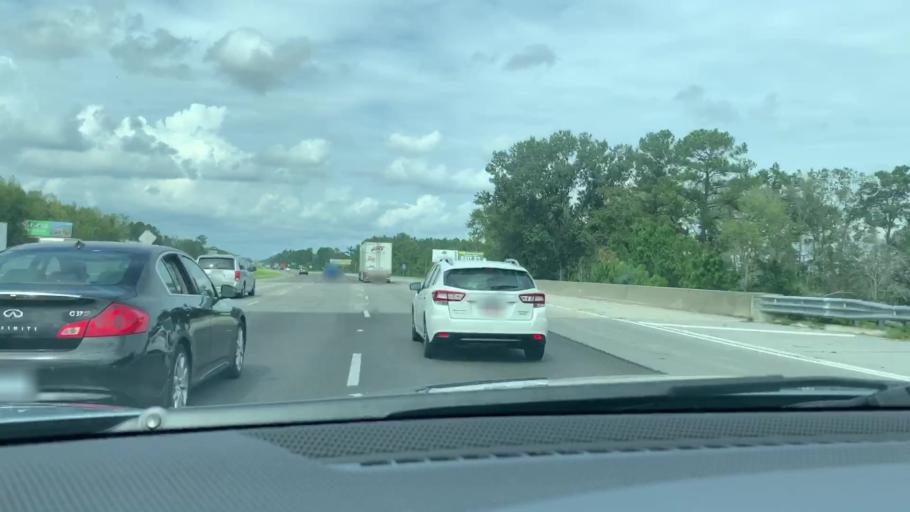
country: US
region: Georgia
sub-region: Liberty County
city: Midway
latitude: 31.6582
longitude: -81.3927
